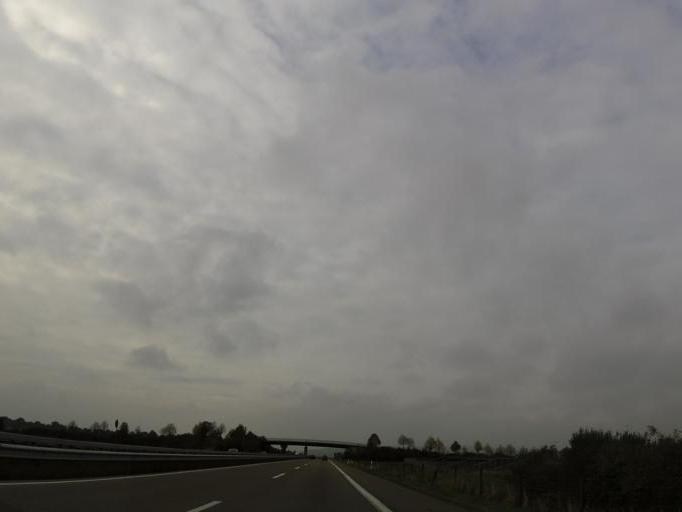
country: DE
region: Rheinland-Pfalz
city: Morschheim
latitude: 49.6912
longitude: 8.0427
